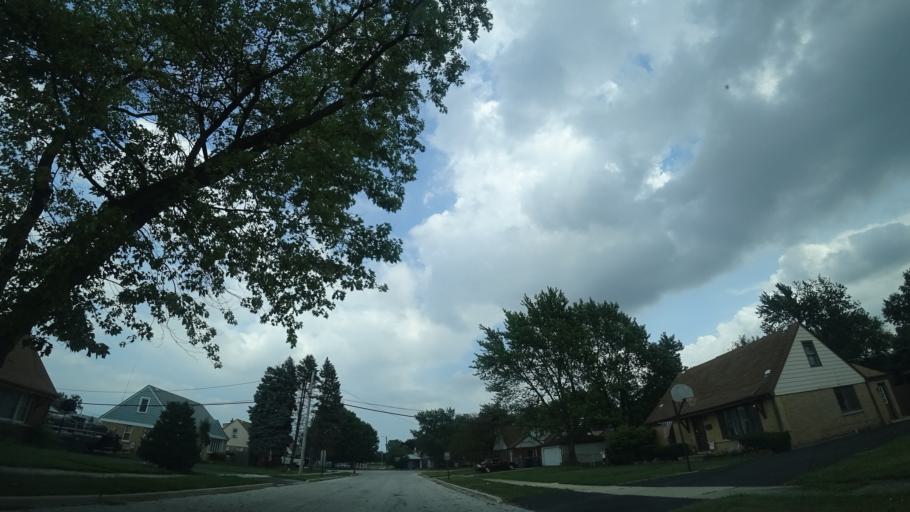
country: US
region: Illinois
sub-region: Cook County
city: Chicago Ridge
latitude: 41.6970
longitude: -87.7665
